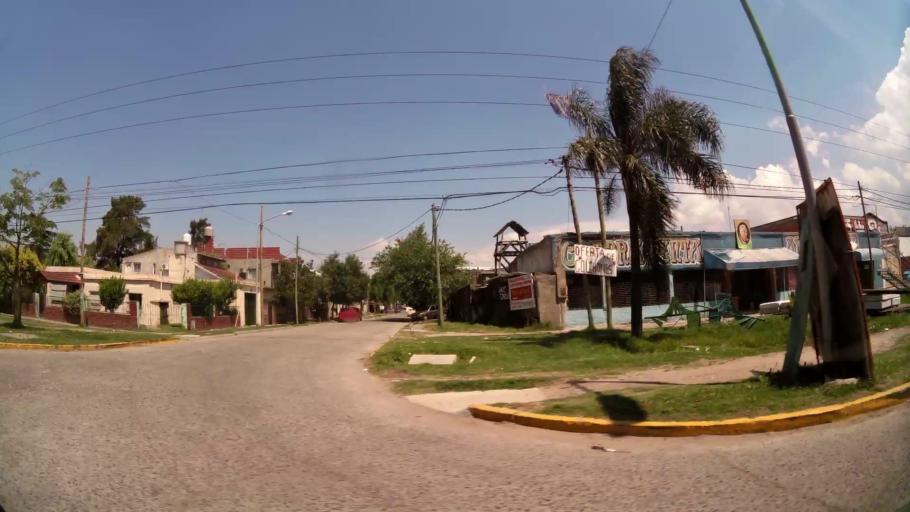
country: AR
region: Buenos Aires
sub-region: Partido de Tigre
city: Tigre
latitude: -34.4421
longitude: -58.5872
